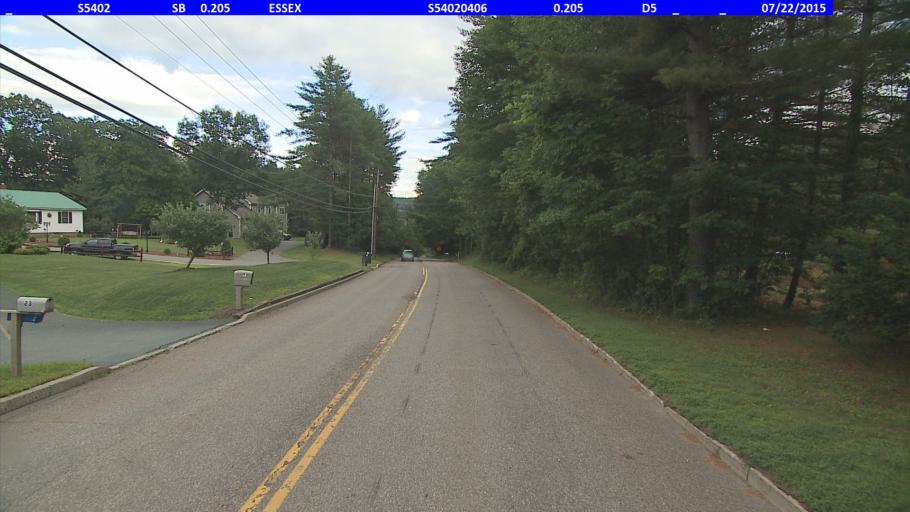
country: US
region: Vermont
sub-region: Chittenden County
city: Williston
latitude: 44.4818
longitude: -73.0501
